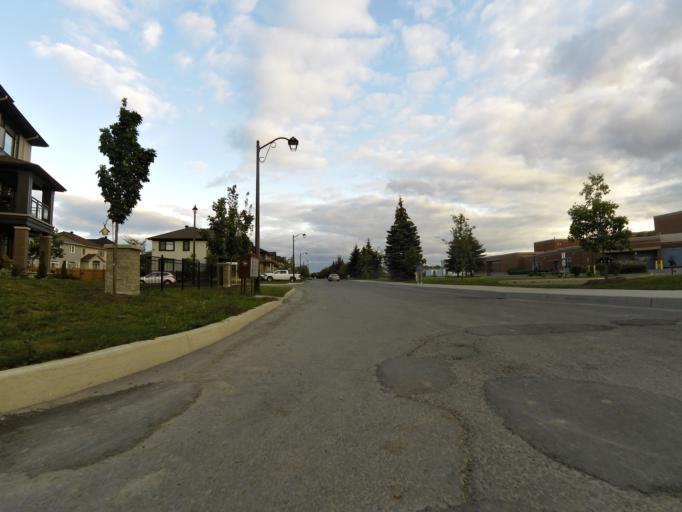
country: CA
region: Ontario
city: Bells Corners
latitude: 45.2860
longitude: -75.7385
